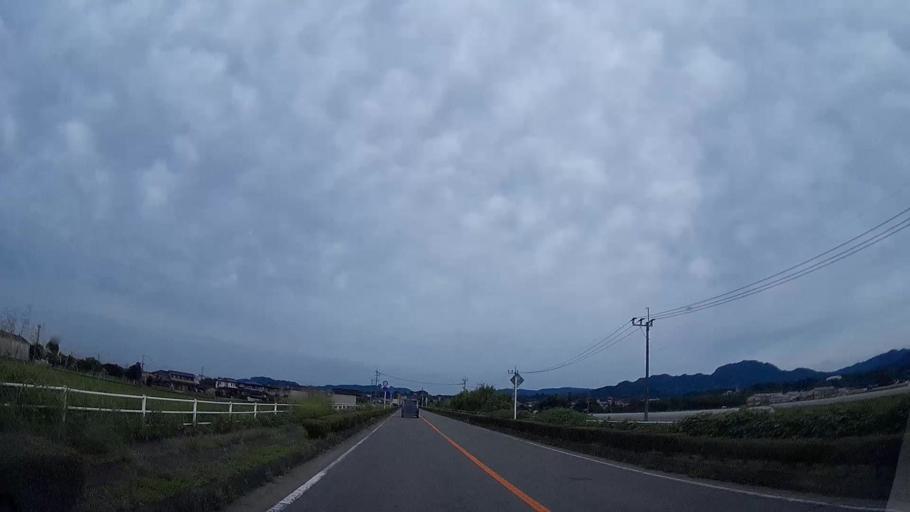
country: JP
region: Kumamoto
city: Kikuchi
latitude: 32.9659
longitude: 130.8135
